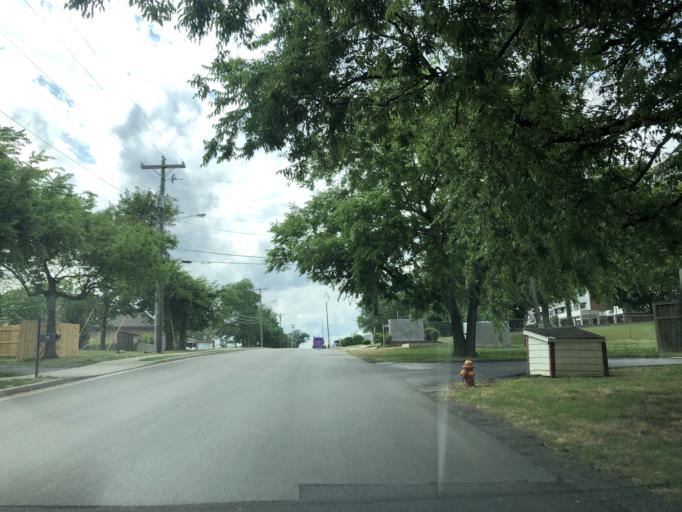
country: US
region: Tennessee
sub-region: Davidson County
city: Goodlettsville
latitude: 36.2673
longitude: -86.6976
